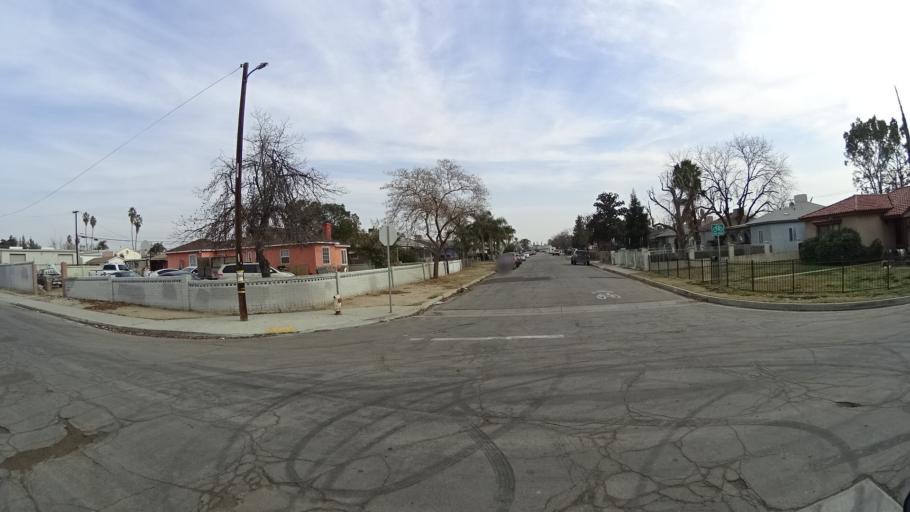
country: US
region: California
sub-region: Kern County
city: Bakersfield
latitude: 35.3762
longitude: -118.9715
